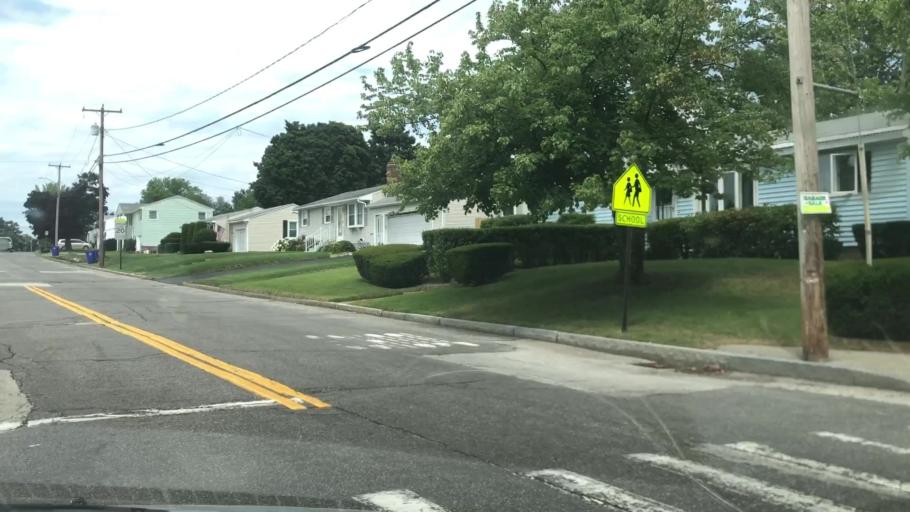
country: US
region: New Hampshire
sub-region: Hillsborough County
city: Manchester
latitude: 42.9647
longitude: -71.4334
